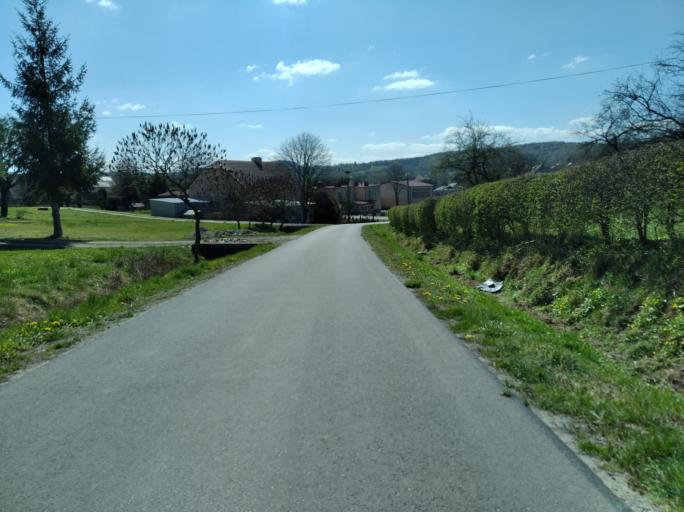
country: PL
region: Subcarpathian Voivodeship
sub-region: Powiat strzyzowski
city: Wisniowa
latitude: 49.9132
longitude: 21.6787
